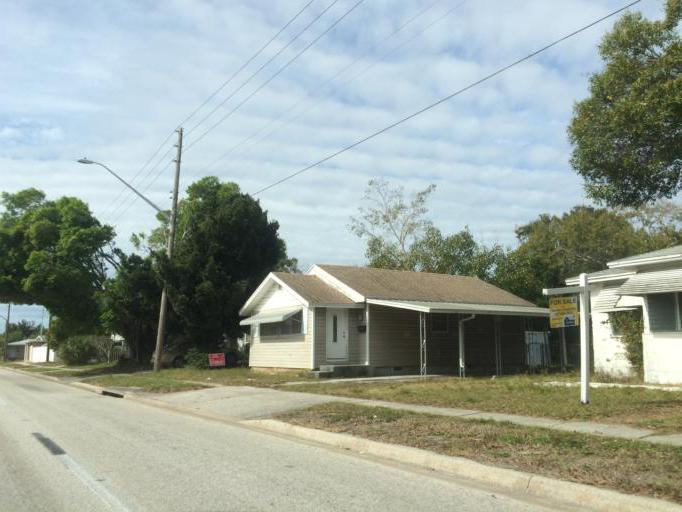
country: US
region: Florida
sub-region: Pinellas County
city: Lealman
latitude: 27.8066
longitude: -82.6679
